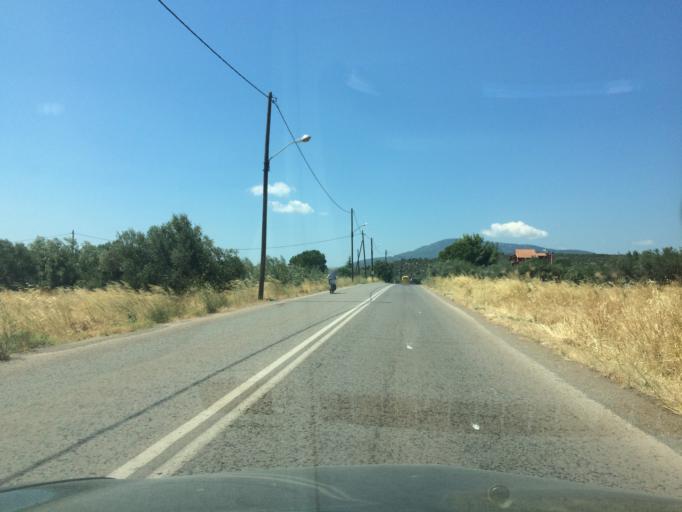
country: GR
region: Central Greece
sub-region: Nomos Evvoias
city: Psachna
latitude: 38.5790
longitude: 23.6266
